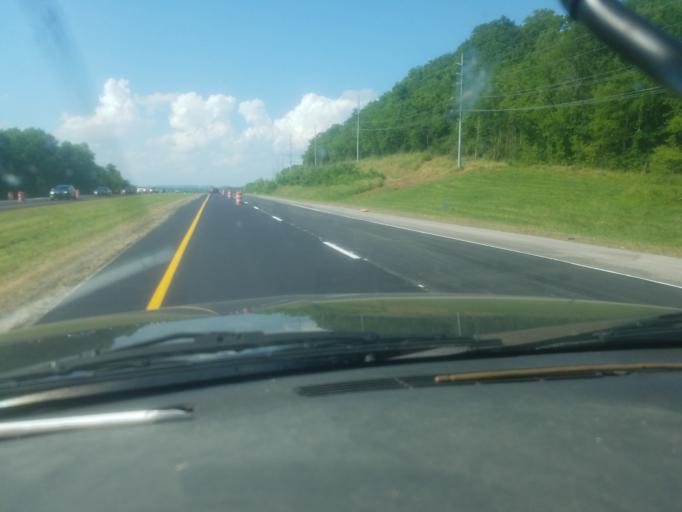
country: US
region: Tennessee
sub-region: Maury County
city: Mount Pleasant
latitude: 35.5364
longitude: -87.2214
